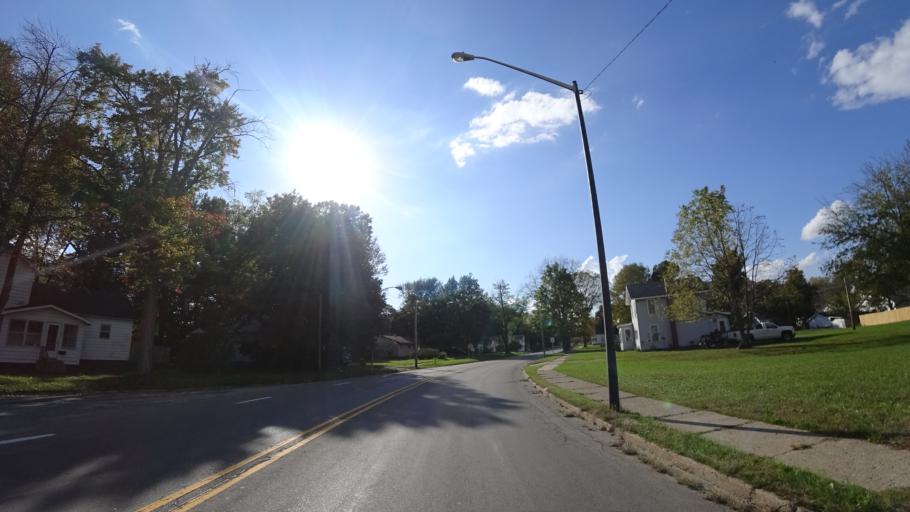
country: US
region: Michigan
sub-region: Saint Joseph County
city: Three Rivers
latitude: 41.9449
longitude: -85.6211
